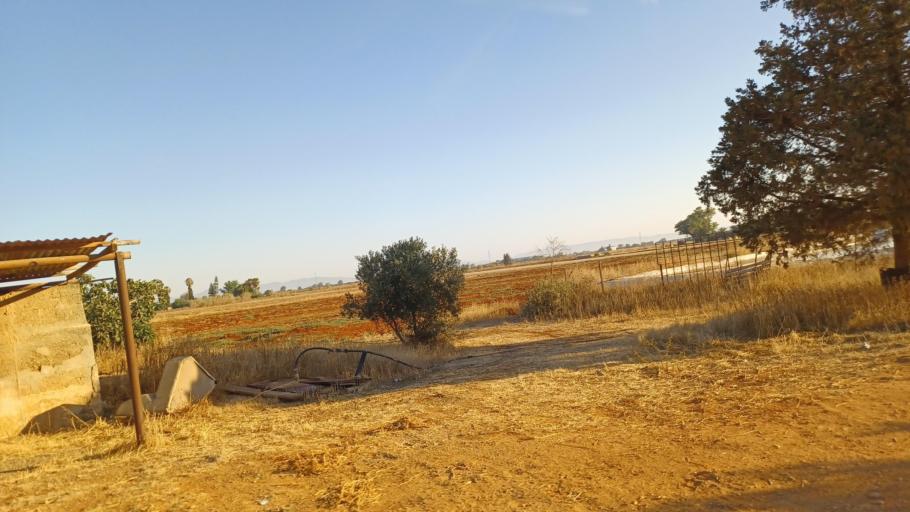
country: CY
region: Ammochostos
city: Avgorou
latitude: 35.0055
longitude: 33.8265
